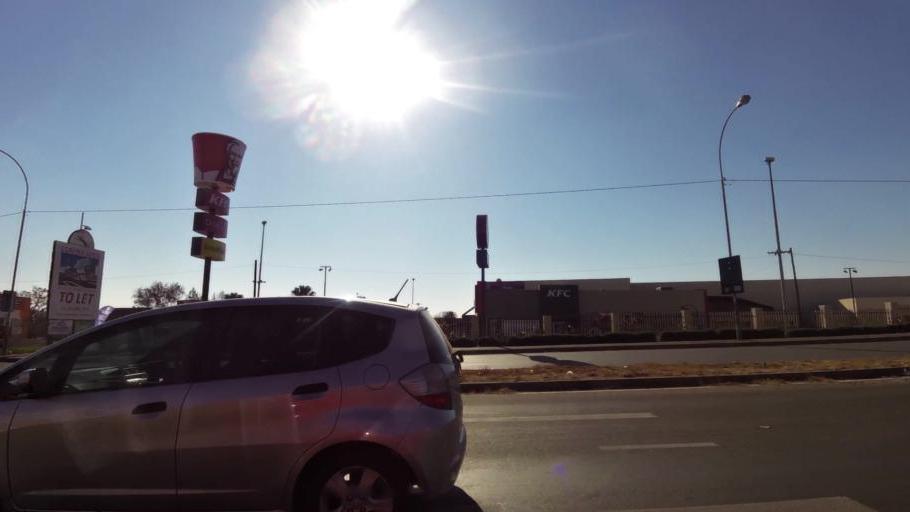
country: ZA
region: Gauteng
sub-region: City of Johannesburg Metropolitan Municipality
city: Johannesburg
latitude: -26.2418
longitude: 28.0044
